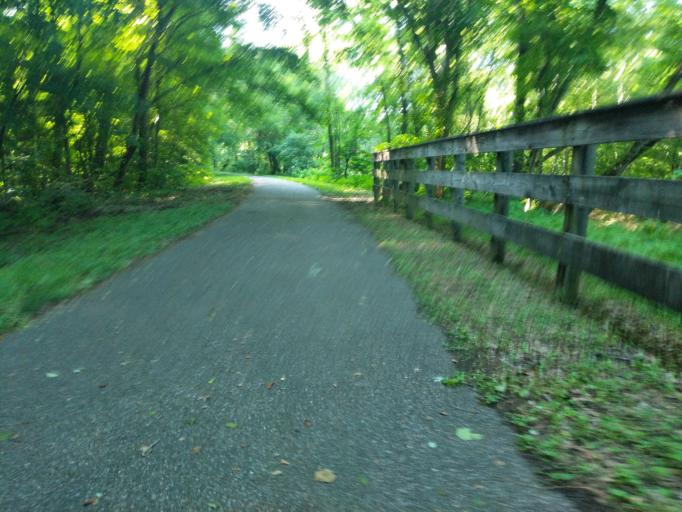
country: US
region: Ohio
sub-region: Athens County
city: Nelsonville
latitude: 39.4253
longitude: -82.1966
